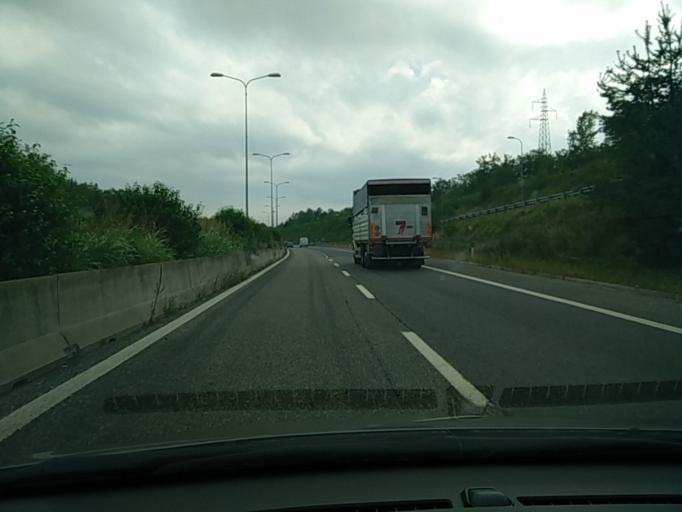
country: IT
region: Lombardy
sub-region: Provincia di Varese
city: Vizzola Ticino
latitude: 45.6231
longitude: 8.7062
